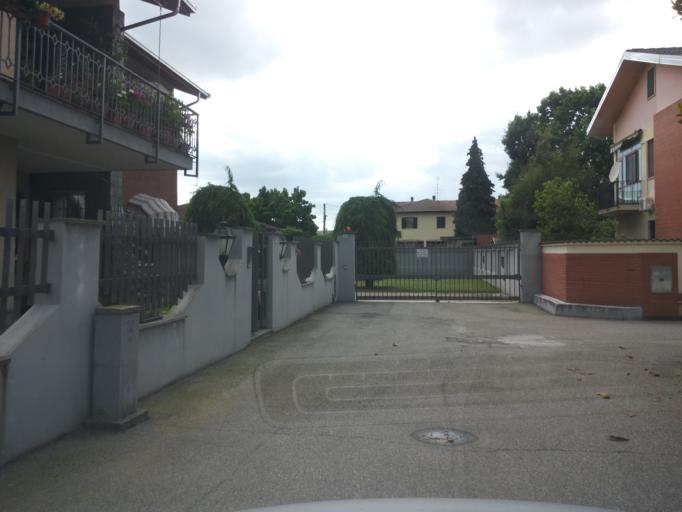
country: IT
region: Piedmont
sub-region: Provincia di Vercelli
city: Borgo Vercelli
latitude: 45.3569
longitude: 8.4718
